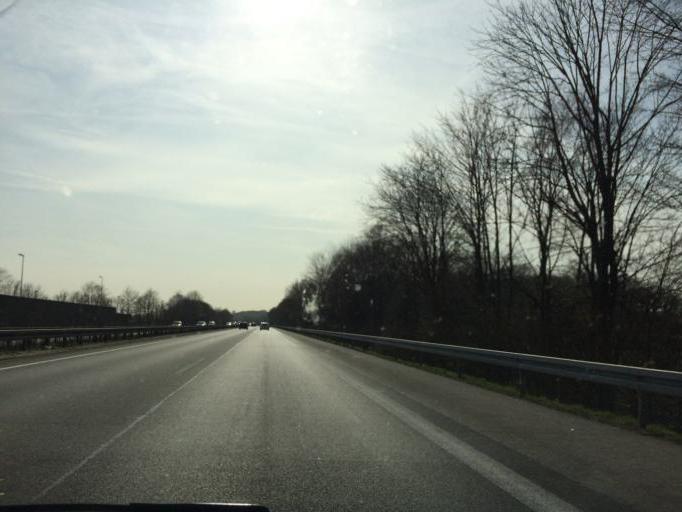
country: DE
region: North Rhine-Westphalia
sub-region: Regierungsbezirk Munster
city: Dulmen
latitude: 51.8696
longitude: 7.3234
